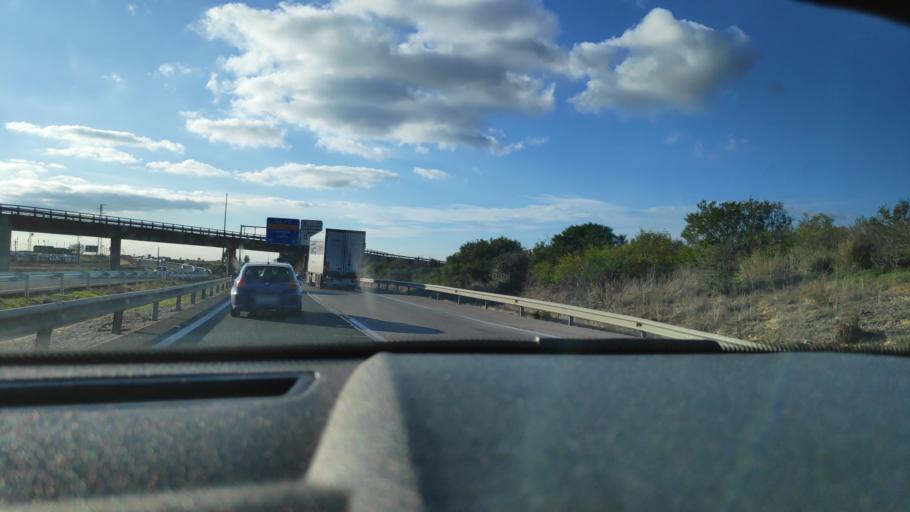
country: ES
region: Andalusia
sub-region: Provincia de Sevilla
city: Carmona
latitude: 37.4725
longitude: -5.6834
